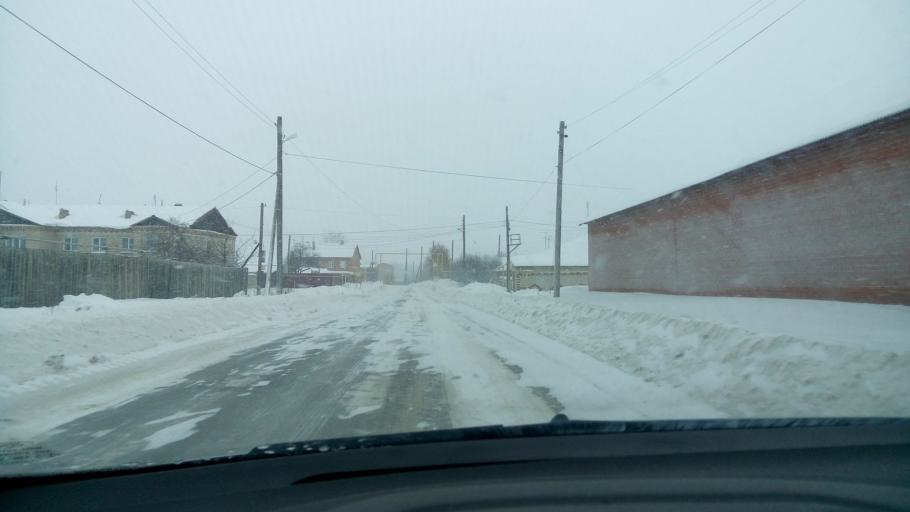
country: RU
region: Sverdlovsk
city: Bogdanovich
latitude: 56.7882
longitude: 62.0534
